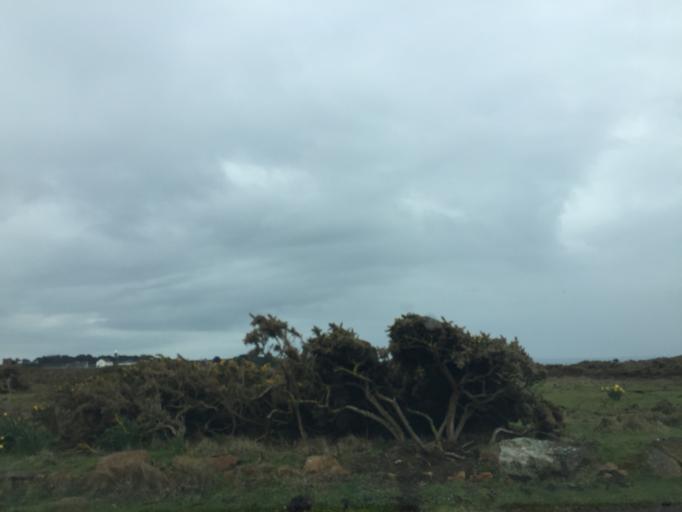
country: JE
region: St Helier
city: Saint Helier
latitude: 49.1813
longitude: -2.2384
